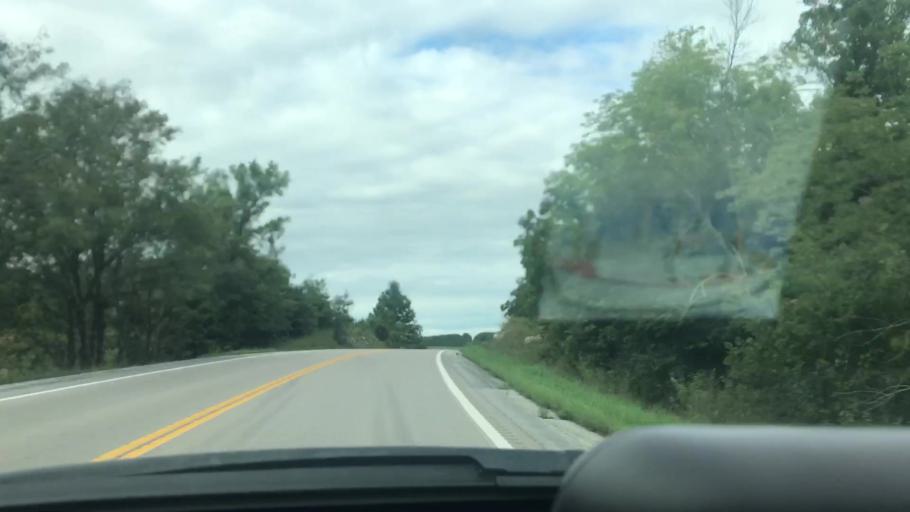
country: US
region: Missouri
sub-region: Benton County
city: Warsaw
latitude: 38.1265
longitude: -93.2805
